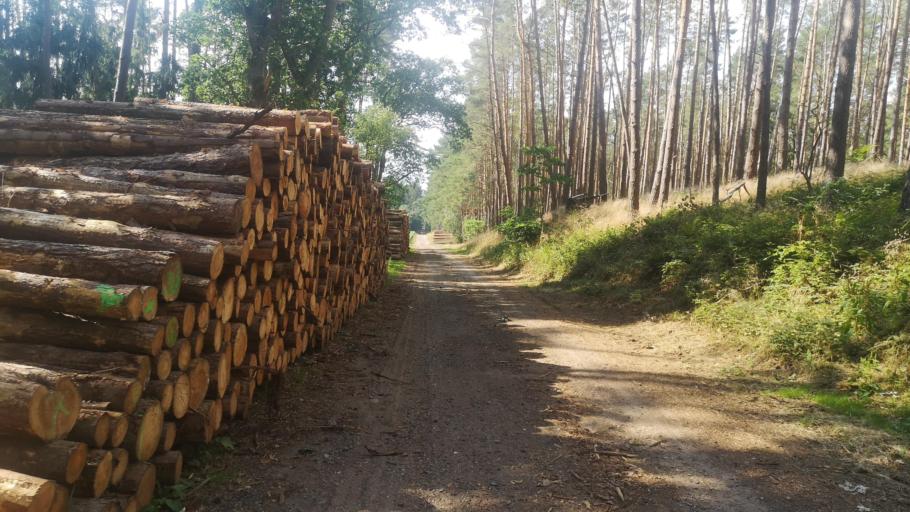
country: DE
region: Lower Saxony
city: Dahlem
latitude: 53.2130
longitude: 10.7378
